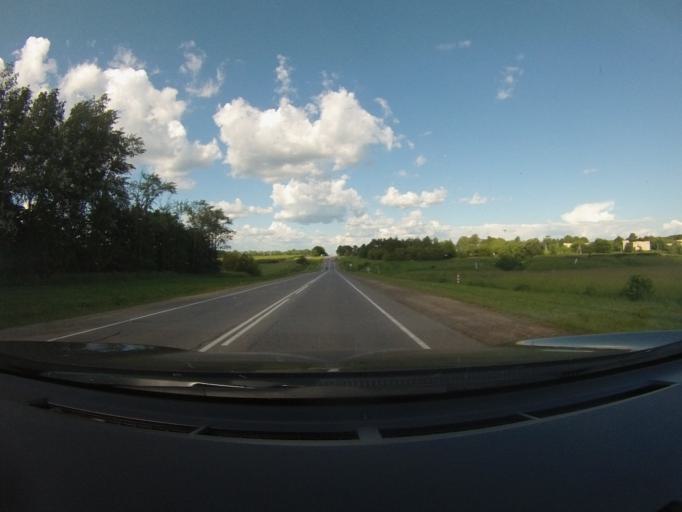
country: RU
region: Tula
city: Bol'shoye Skuratovo
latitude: 53.4427
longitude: 36.8312
